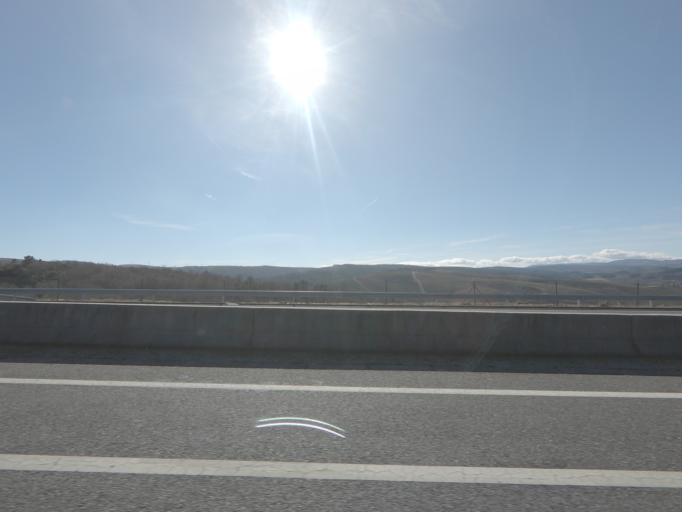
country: ES
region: Galicia
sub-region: Provincia de Pontevedra
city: Dozon
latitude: 42.5802
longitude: -8.0664
